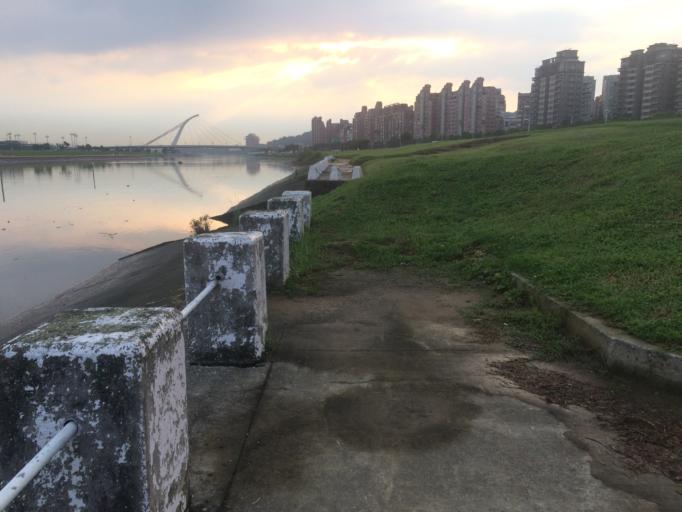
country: TW
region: Taipei
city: Taipei
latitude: 25.0758
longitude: 121.5553
